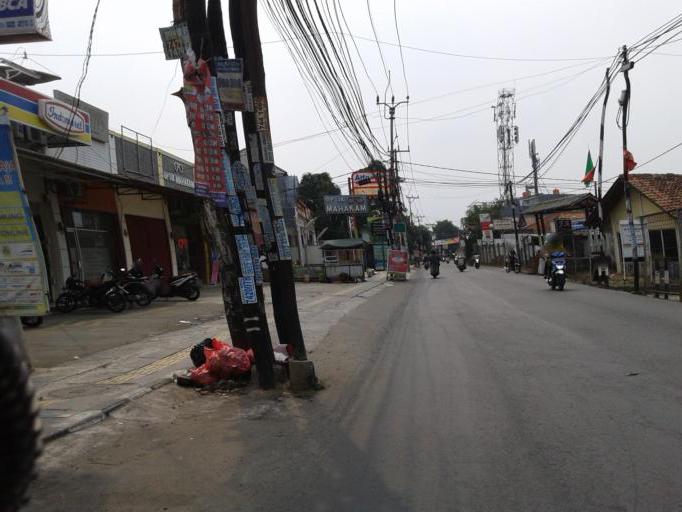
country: ID
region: Banten
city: South Tangerang
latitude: -6.3036
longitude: 106.7535
